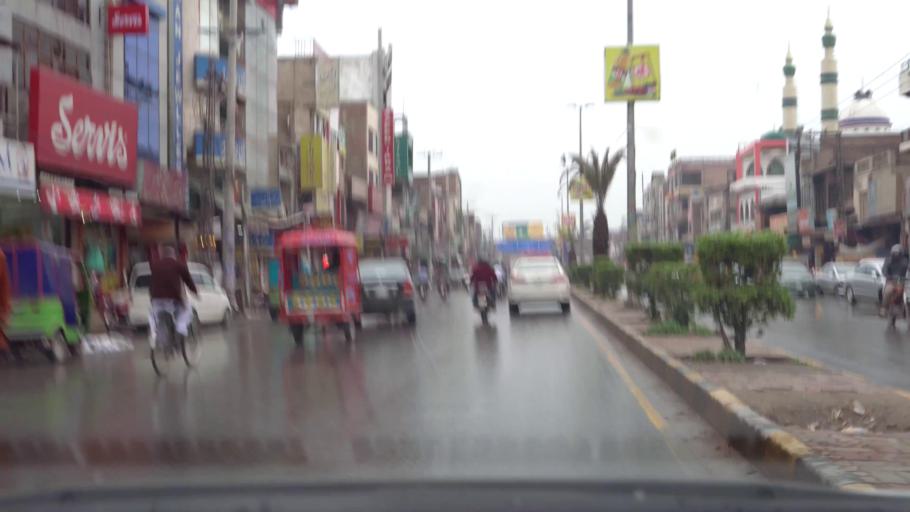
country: PK
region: Punjab
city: Faisalabad
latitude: 31.4072
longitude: 73.0994
